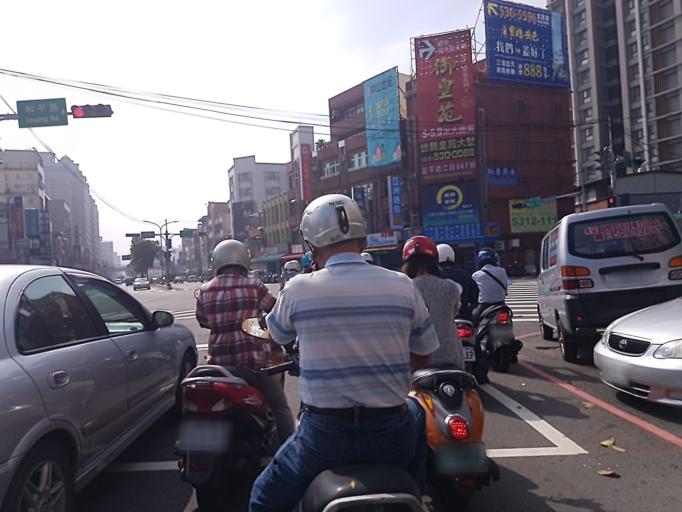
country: TW
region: Taiwan
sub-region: Hsinchu
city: Hsinchu
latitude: 24.8067
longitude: 120.9563
